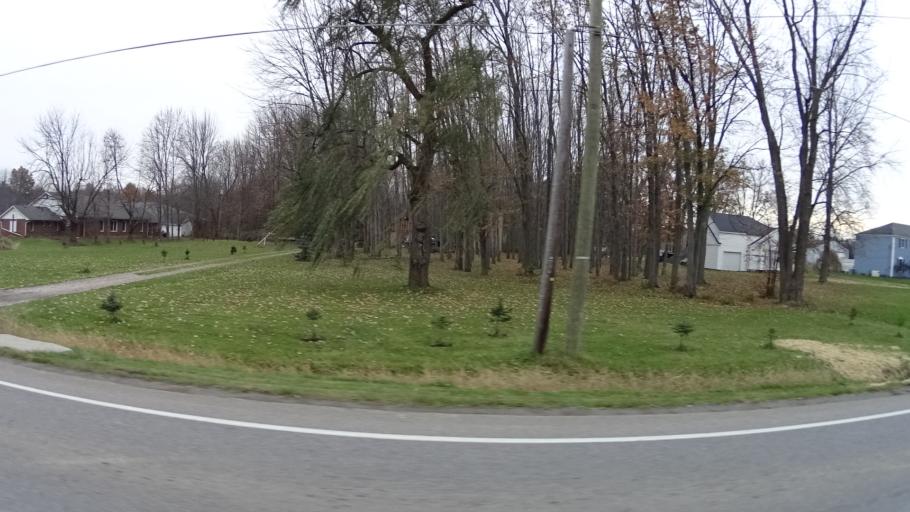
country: US
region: Ohio
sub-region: Lorain County
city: Elyria
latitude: 41.3250
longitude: -82.1176
